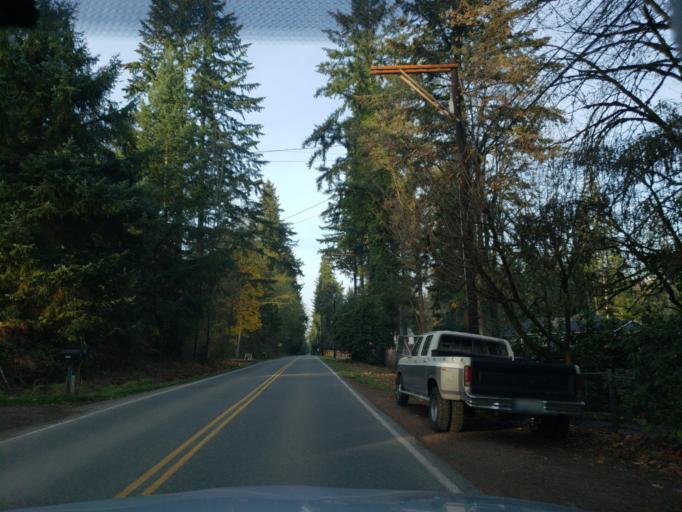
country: US
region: Washington
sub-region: Snohomish County
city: Maltby
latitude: 47.7829
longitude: -122.1324
